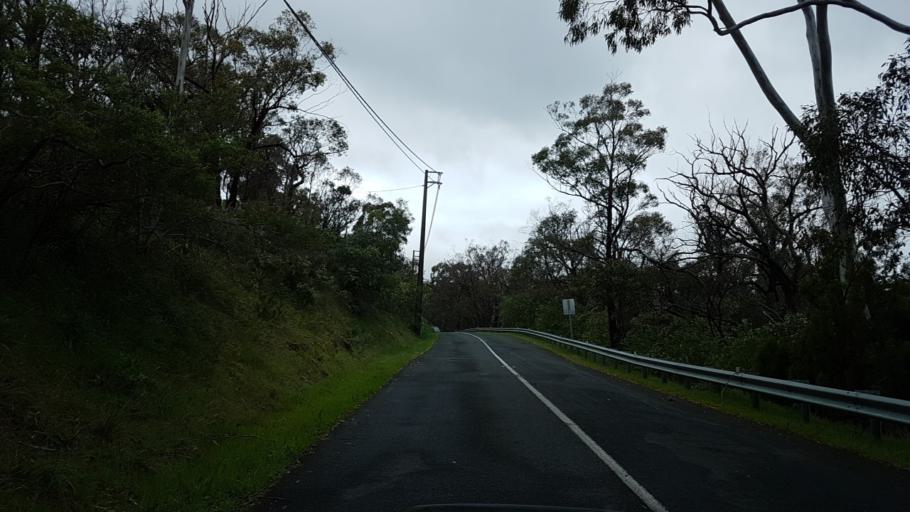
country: AU
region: South Australia
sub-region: Adelaide Hills
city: Adelaide Hills
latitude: -34.9014
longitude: 138.7627
